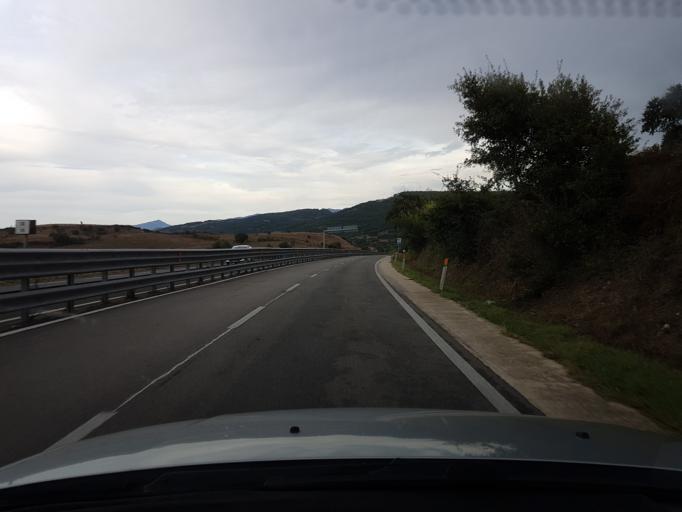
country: IT
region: Sardinia
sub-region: Provincia di Oristano
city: Sedilo
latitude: 40.1804
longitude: 8.9475
